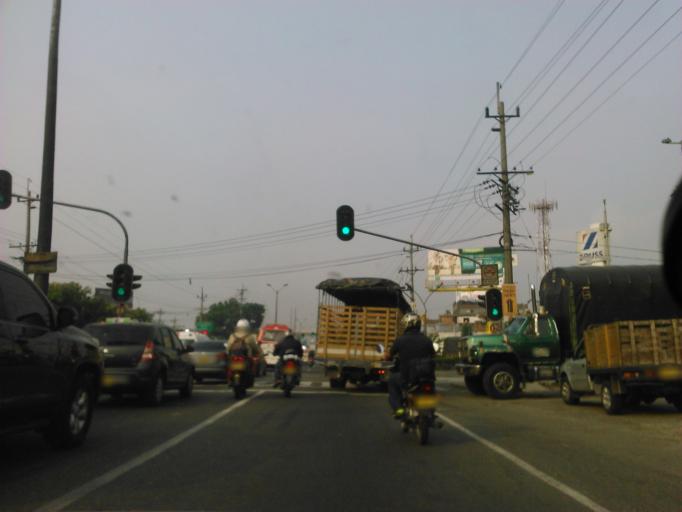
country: CO
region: Antioquia
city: Envigado
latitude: 6.1683
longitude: -75.6065
